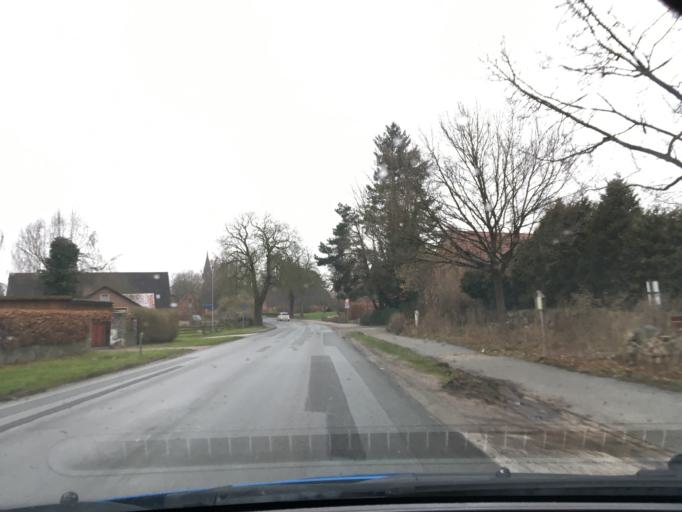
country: DE
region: Schleswig-Holstein
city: Breitenfelde
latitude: 53.6031
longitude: 10.6406
